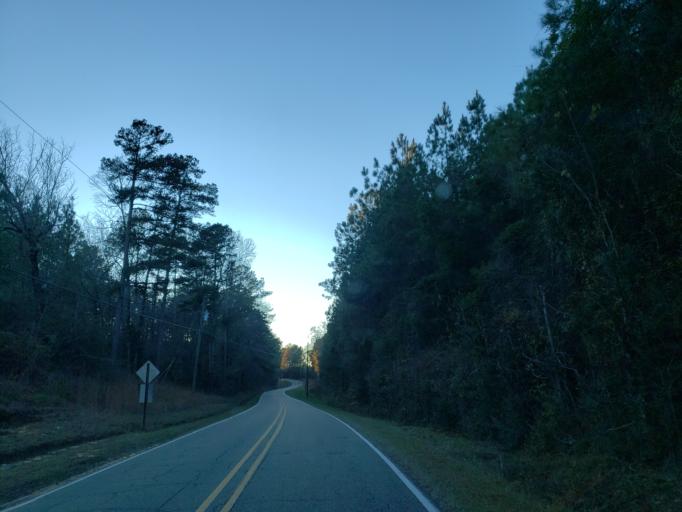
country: US
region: Mississippi
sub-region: Forrest County
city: Rawls Springs
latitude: 31.4303
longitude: -89.3248
